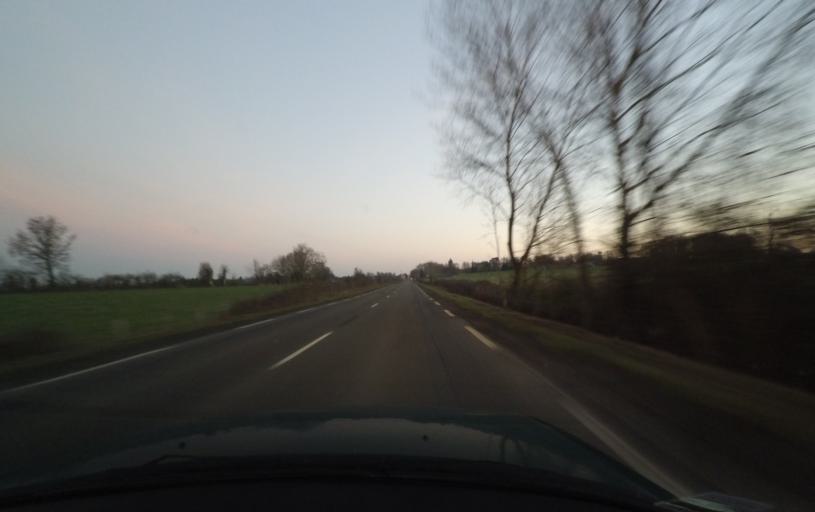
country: FR
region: Pays de la Loire
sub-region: Departement de la Mayenne
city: Soulge-sur-Ouette
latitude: 48.0522
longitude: -0.5719
